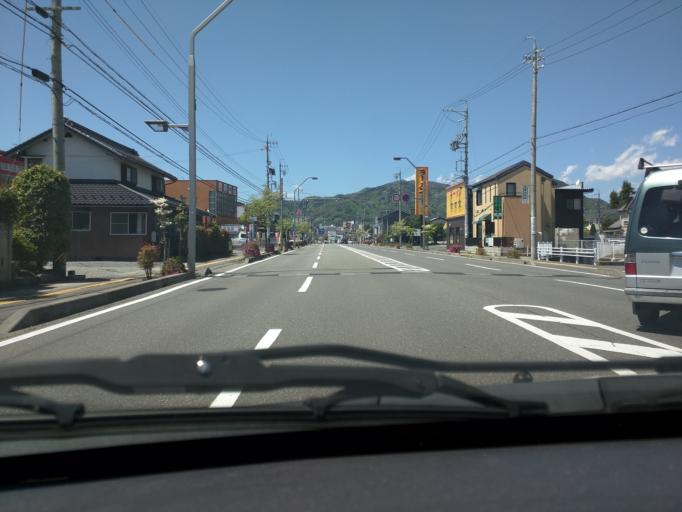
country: JP
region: Nagano
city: Nagano-shi
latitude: 36.6425
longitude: 138.2055
